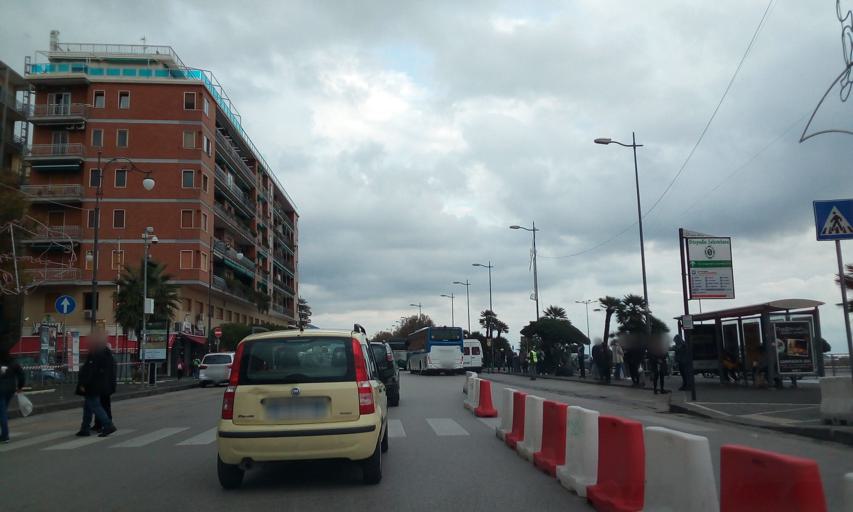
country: IT
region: Campania
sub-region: Provincia di Salerno
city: Salerno
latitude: 40.6743
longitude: 14.7696
